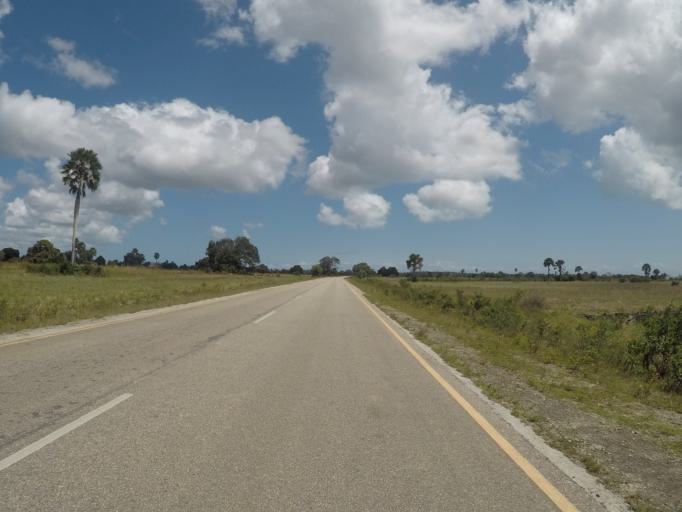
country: TZ
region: Zanzibar Central/South
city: Koani
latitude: -6.2142
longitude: 39.3650
